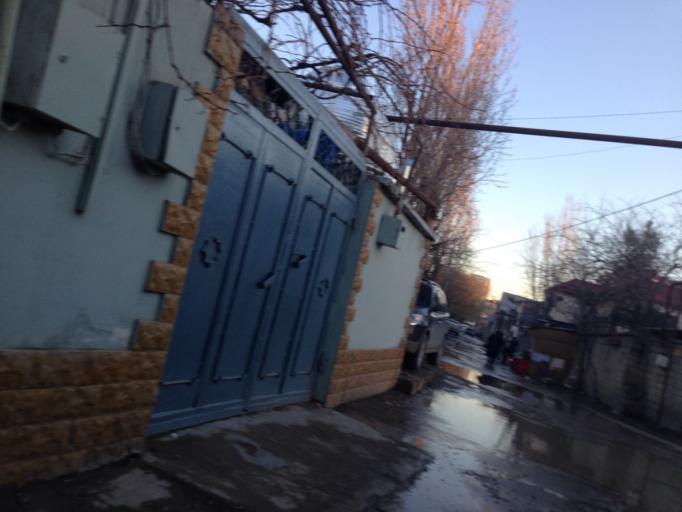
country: AZ
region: Baki
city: Baku
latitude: 40.4144
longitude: 49.8642
